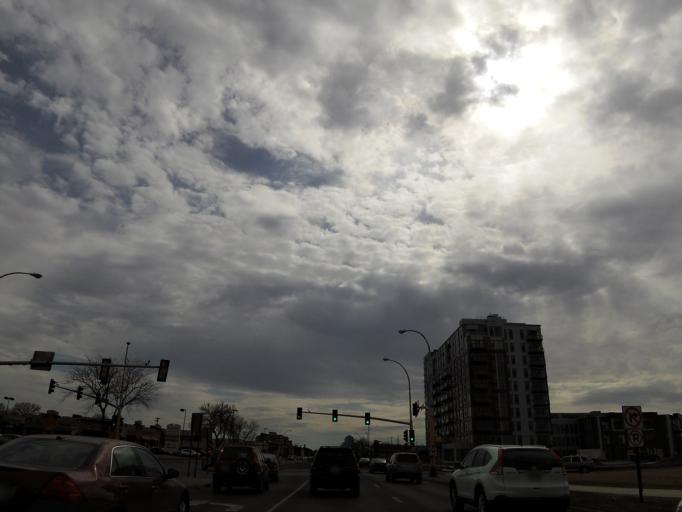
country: US
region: Minnesota
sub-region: Hennepin County
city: Edina
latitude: 44.8804
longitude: -93.3214
